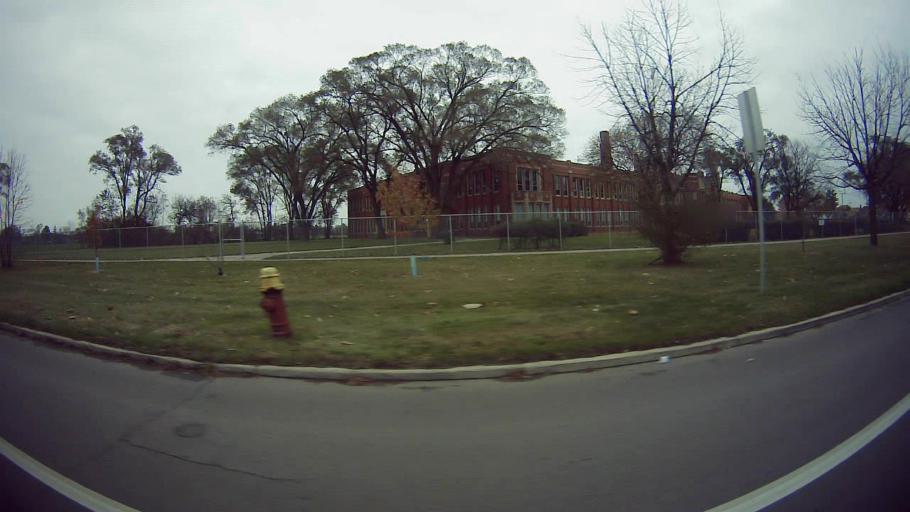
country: US
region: Michigan
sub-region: Wayne County
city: Hamtramck
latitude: 42.4123
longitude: -83.0592
